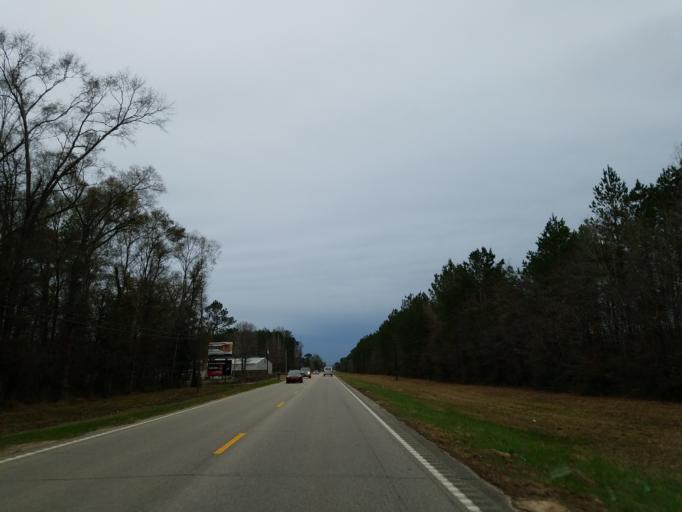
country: US
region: Mississippi
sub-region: Forrest County
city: Glendale
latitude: 31.4260
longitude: -89.2814
